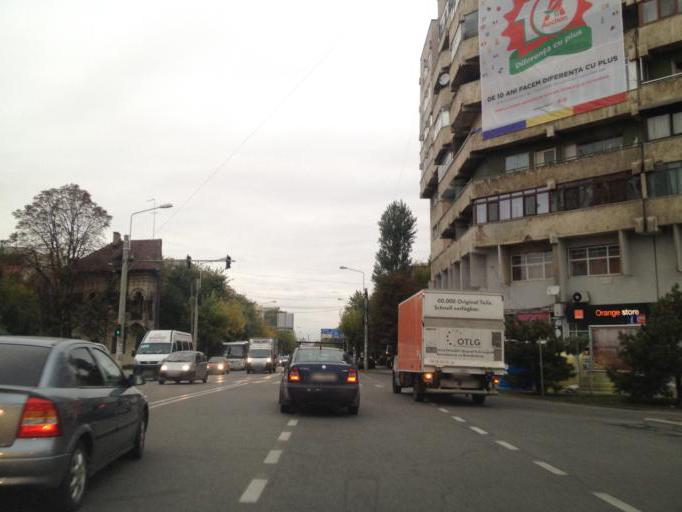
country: RO
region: Dolj
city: Craiova
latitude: 44.3281
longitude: 23.8152
